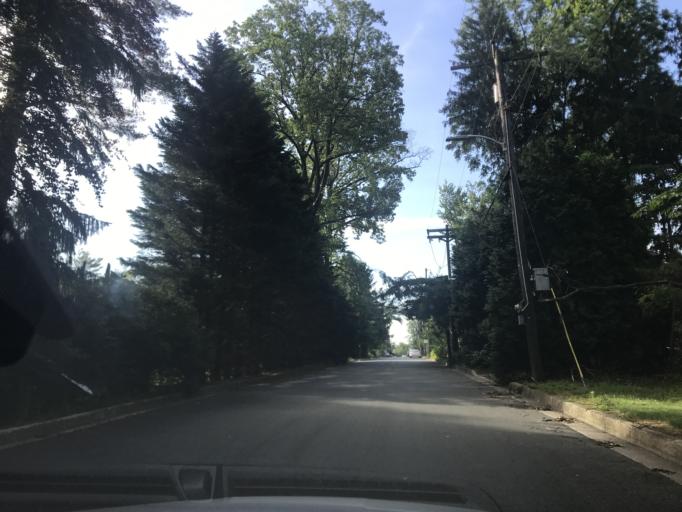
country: US
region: Maryland
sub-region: Harford County
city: North Bel Air
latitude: 39.5425
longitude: -76.3536
